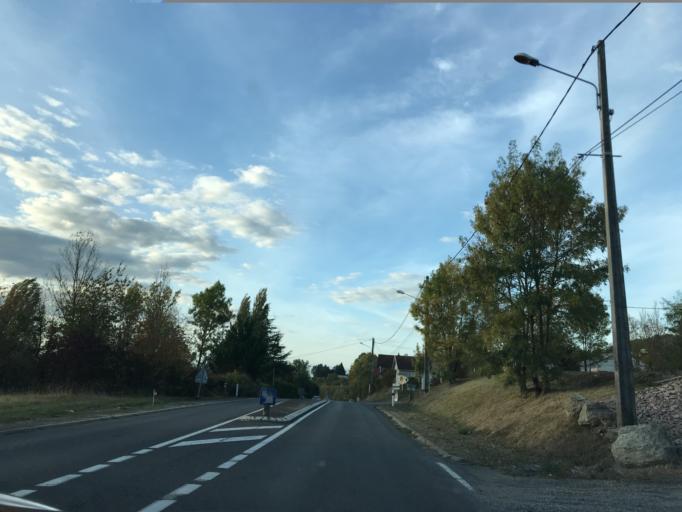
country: FR
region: Auvergne
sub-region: Departement de l'Allier
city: Hauterive
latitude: 46.0861
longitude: 3.4589
